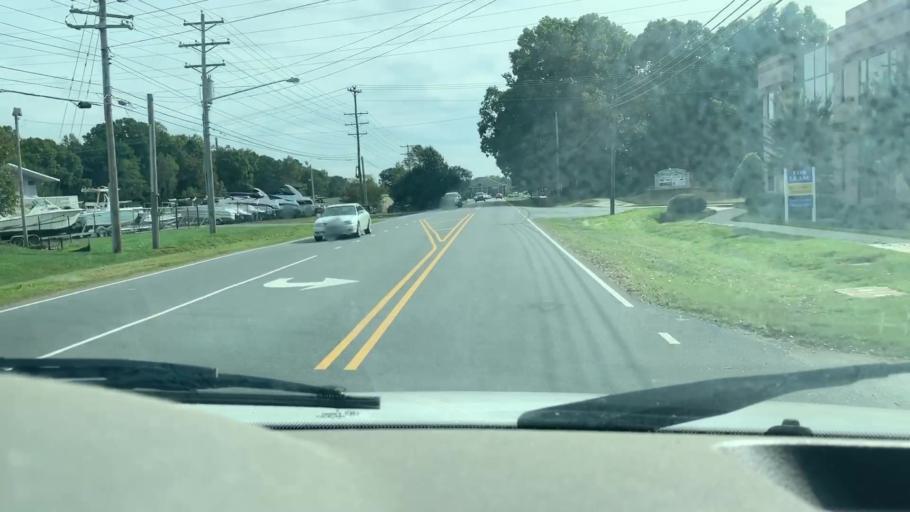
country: US
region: North Carolina
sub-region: Mecklenburg County
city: Cornelius
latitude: 35.4741
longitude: -80.8916
